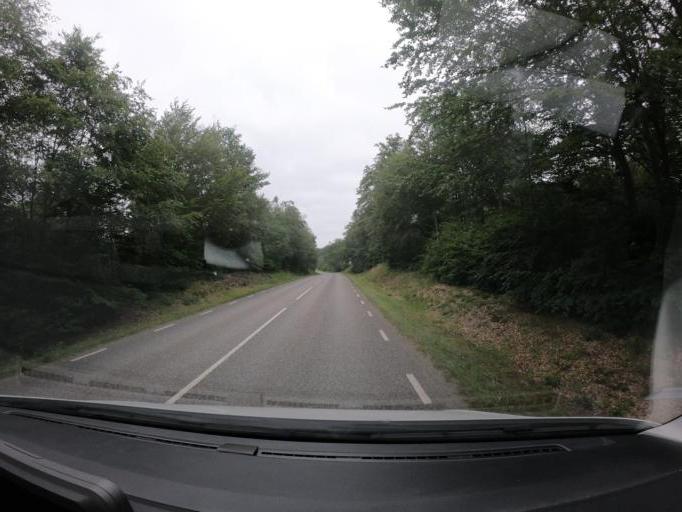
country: SE
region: Skane
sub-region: Perstorps Kommun
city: Perstorp
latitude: 56.1108
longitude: 13.4143
